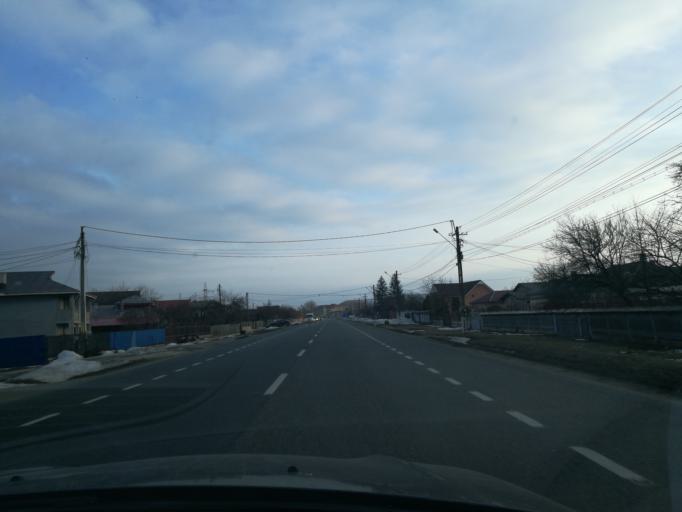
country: RO
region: Bacau
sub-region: Comuna Racaciuni
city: Racaciuni
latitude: 46.3392
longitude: 27.0007
